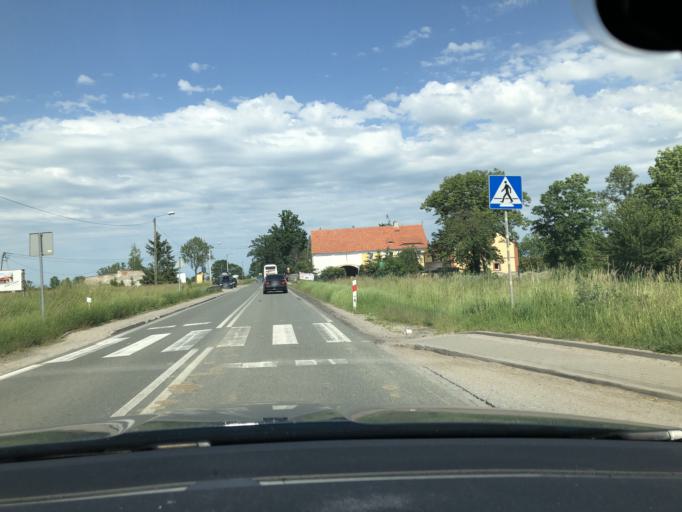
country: PL
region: Lower Silesian Voivodeship
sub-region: Powiat jaworski
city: Paszowice
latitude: 50.9773
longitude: 16.1589
